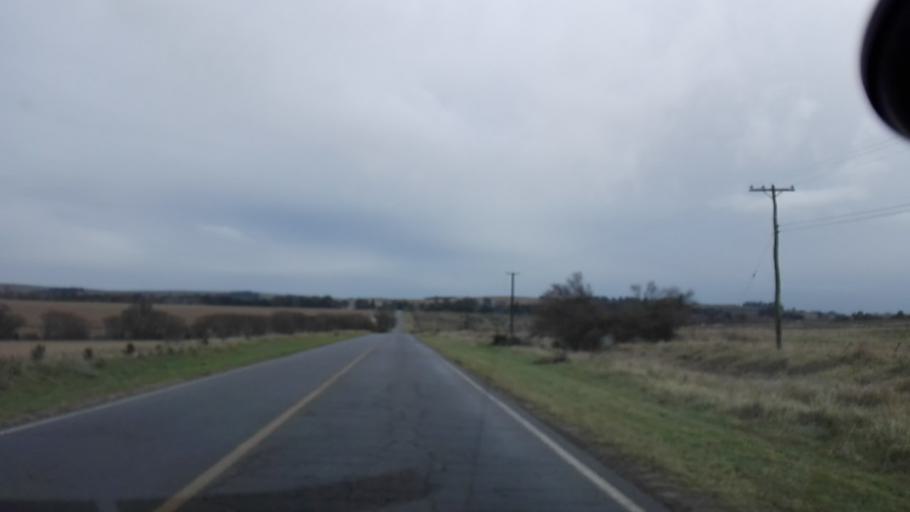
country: AR
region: Buenos Aires
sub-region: Partido de Tandil
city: Tandil
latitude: -37.3582
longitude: -59.1857
